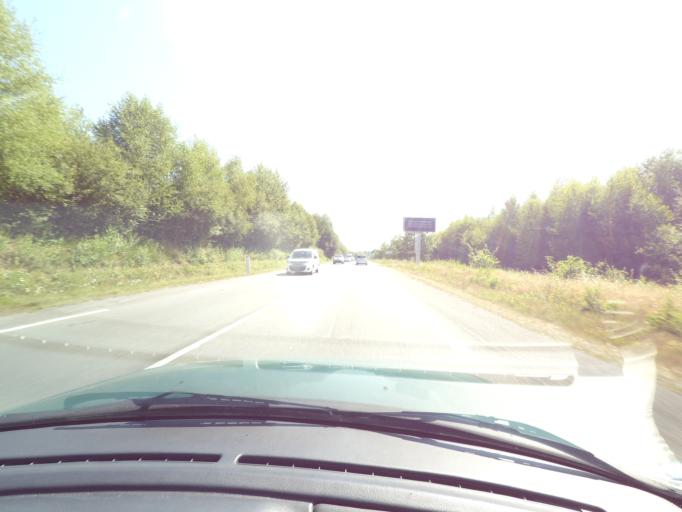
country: FR
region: Limousin
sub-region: Departement de la Haute-Vienne
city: Chaptelat
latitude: 45.8904
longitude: 1.2726
